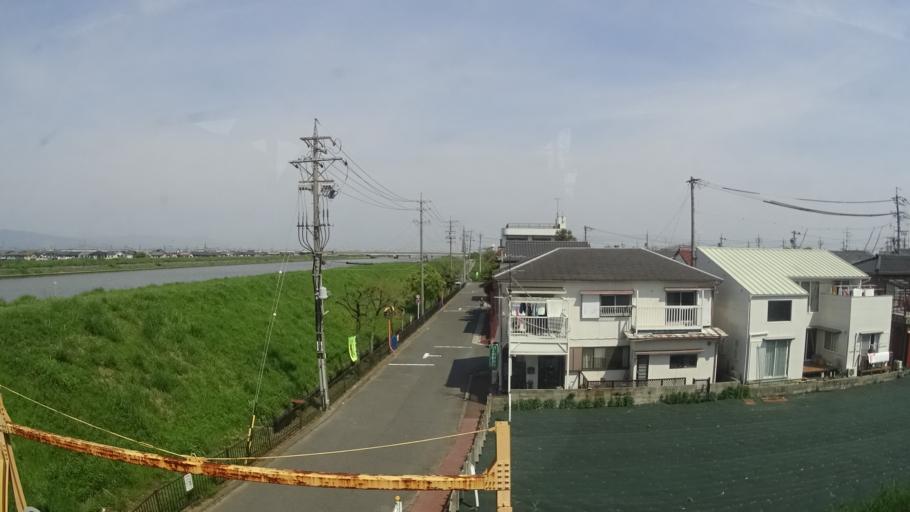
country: JP
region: Aichi
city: Kanie
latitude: 35.1366
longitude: 136.7726
